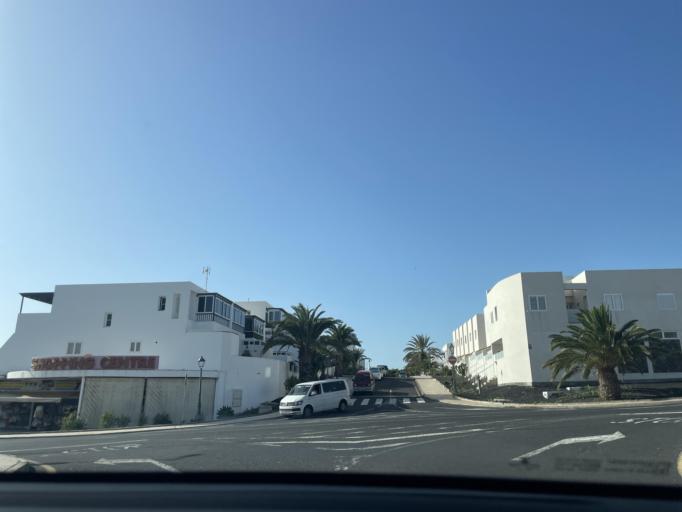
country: ES
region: Canary Islands
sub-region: Provincia de Las Palmas
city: Arrecife
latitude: 28.9963
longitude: -13.4968
